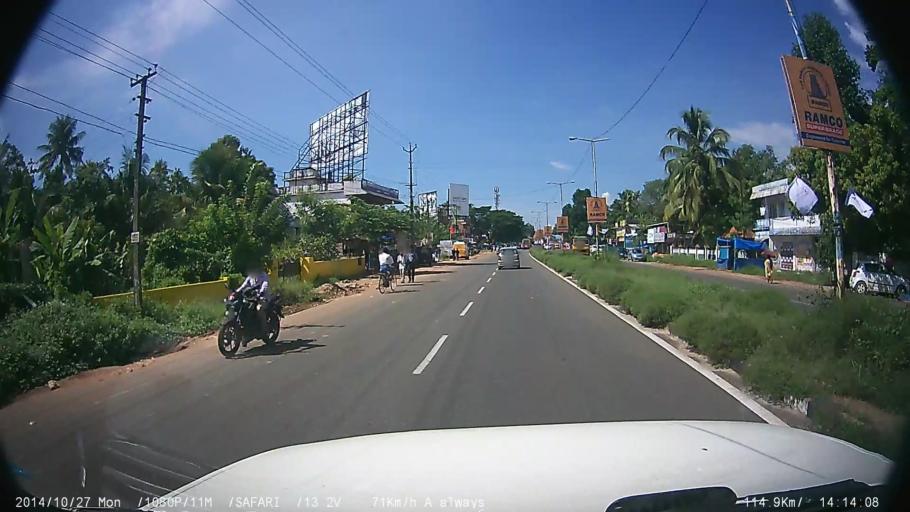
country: IN
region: Kerala
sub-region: Alappuzha
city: Kutiatodu
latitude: 9.8200
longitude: 76.3122
